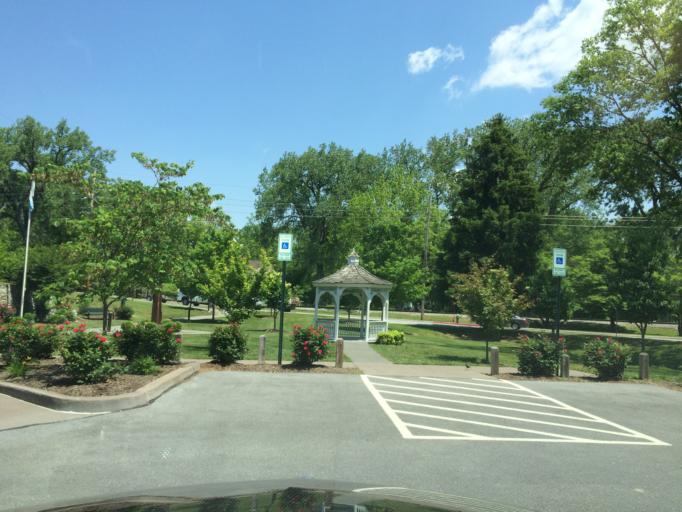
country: US
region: Maryland
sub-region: Washington County
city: Hagerstown
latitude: 39.6387
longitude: -77.7309
